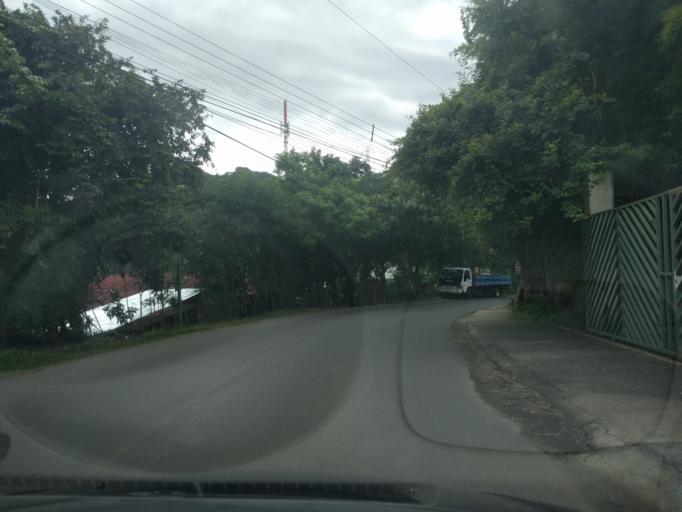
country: CR
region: Heredia
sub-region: Canton de Belen
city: San Antonio
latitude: 9.9643
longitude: -84.1878
